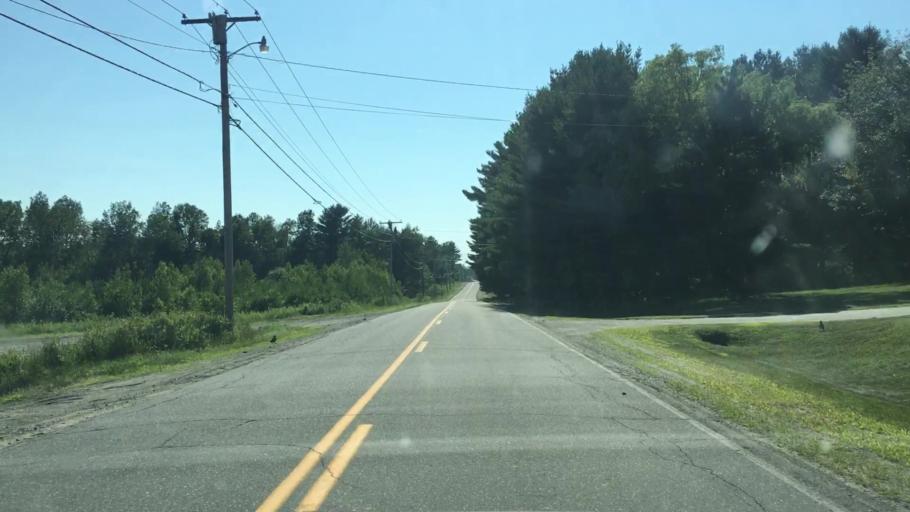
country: US
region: Maine
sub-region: Penobscot County
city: Enfield
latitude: 45.2468
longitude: -68.5974
